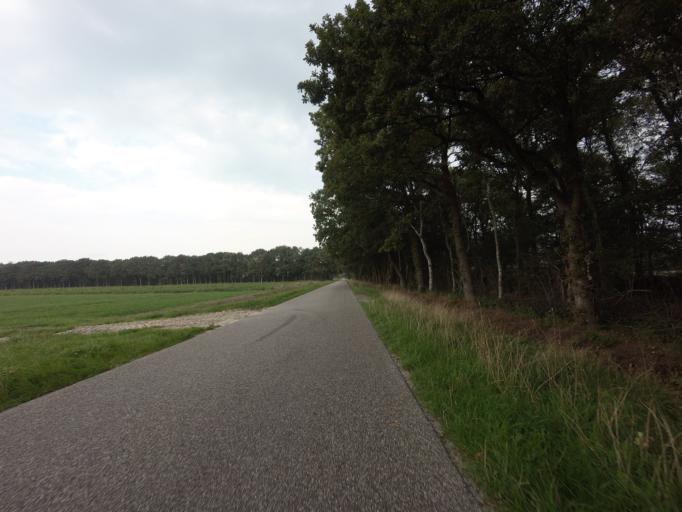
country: NL
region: Drenthe
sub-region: Gemeente Tynaarlo
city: Vries
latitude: 53.0581
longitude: 6.5871
